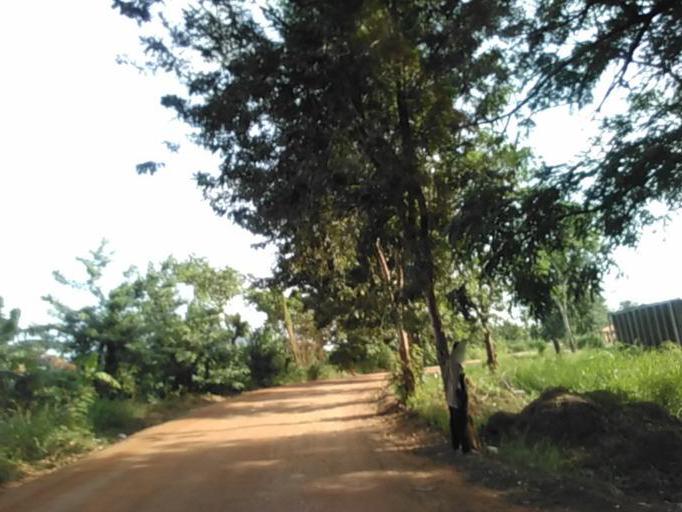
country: GH
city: Akropong
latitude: 6.0944
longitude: 0.2000
